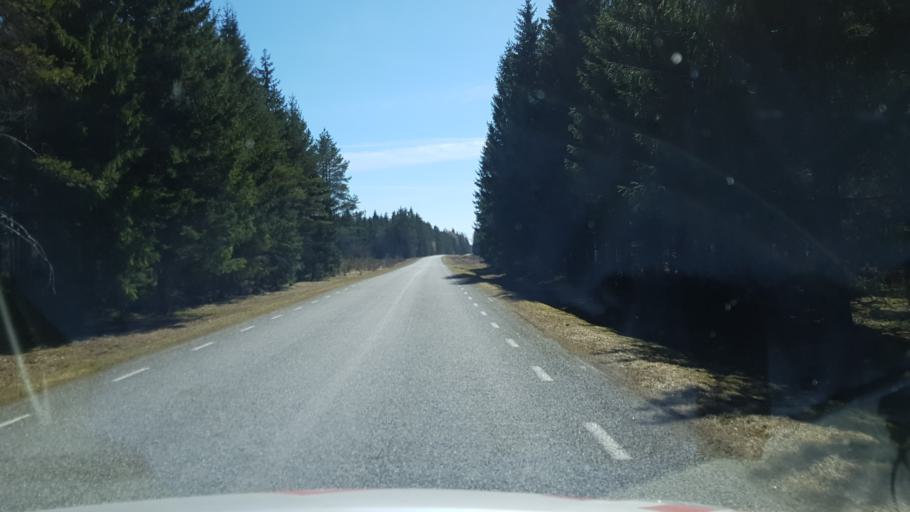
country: EE
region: Laeaene-Virumaa
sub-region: Vinni vald
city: Vinni
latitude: 59.1763
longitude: 26.5037
